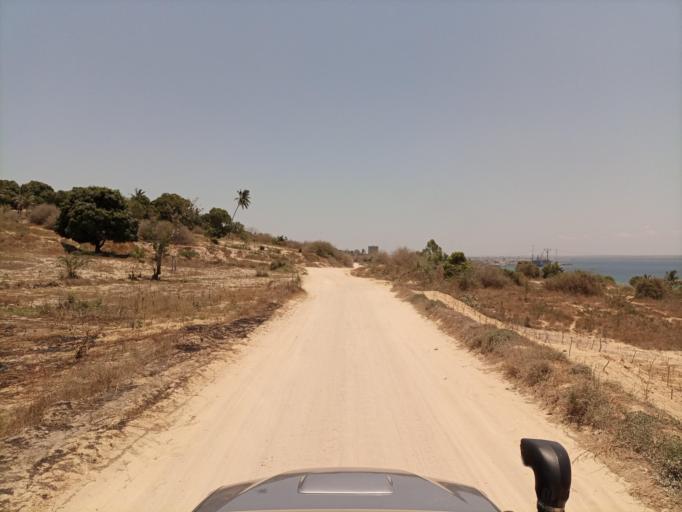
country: MZ
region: Nampula
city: Nacala
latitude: -14.5225
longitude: 40.6791
